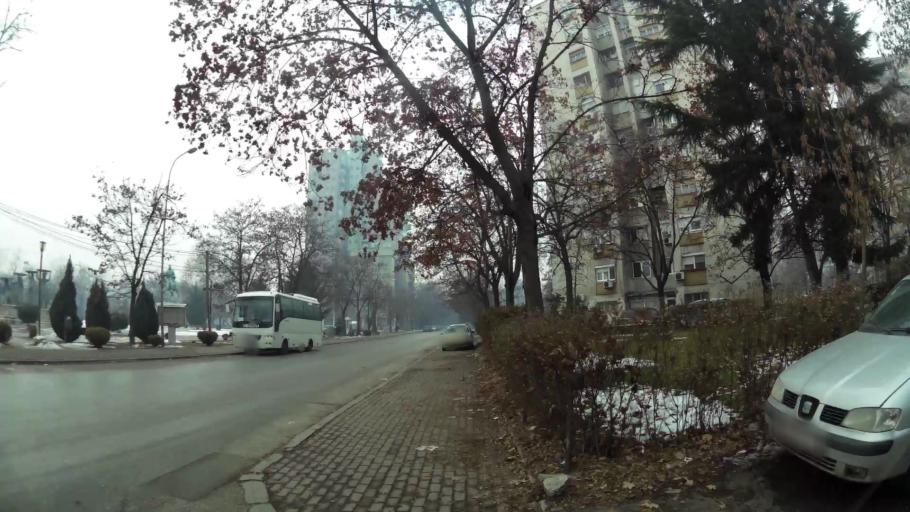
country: MK
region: Cair
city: Cair
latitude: 42.0018
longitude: 21.4625
